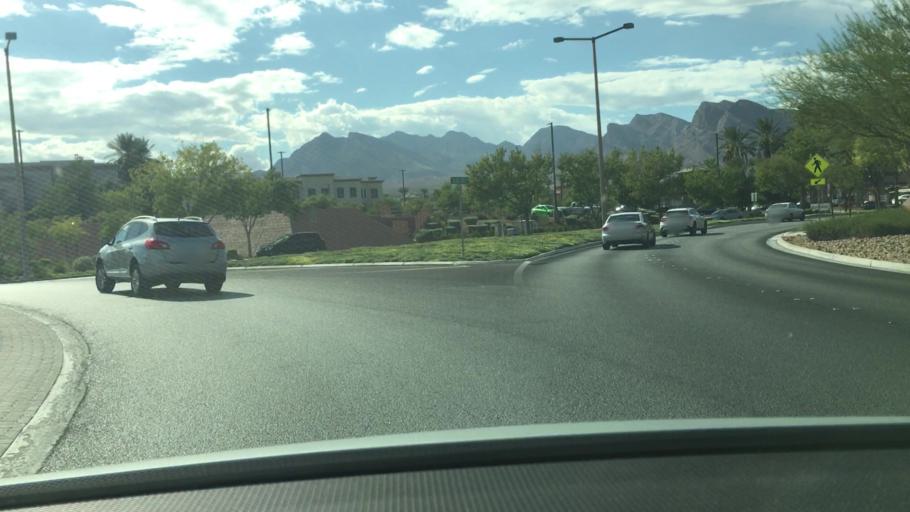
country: US
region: Nevada
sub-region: Clark County
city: Summerlin South
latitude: 36.1899
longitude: -115.3035
